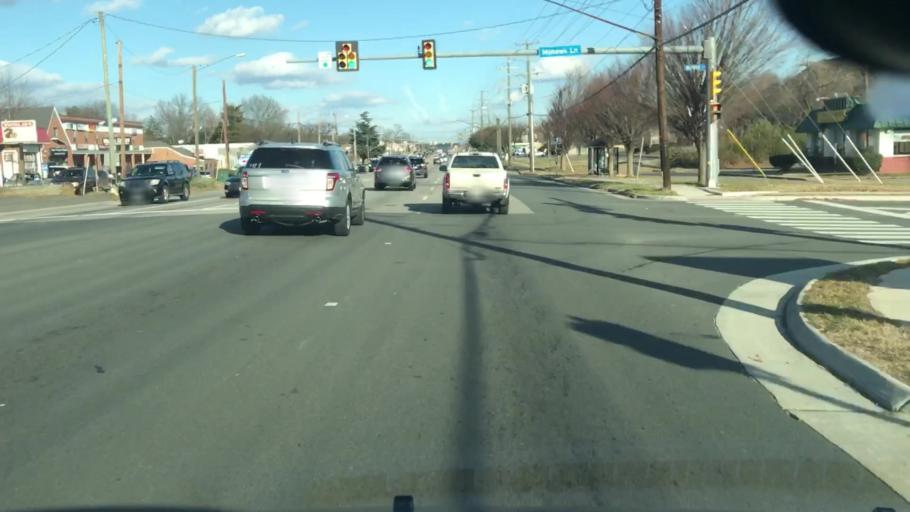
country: US
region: Virginia
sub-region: Fairfax County
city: Mount Vernon
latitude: 38.7313
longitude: -77.1036
